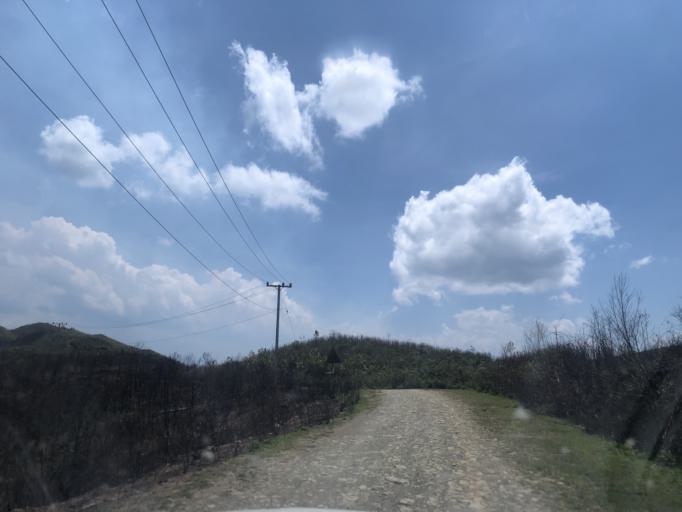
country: LA
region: Phongsali
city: Phongsali
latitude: 21.4091
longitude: 102.1868
